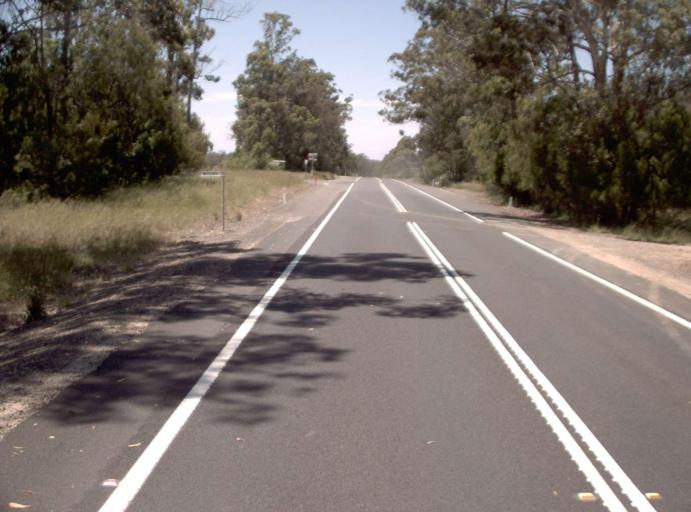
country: AU
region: Victoria
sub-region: East Gippsland
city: Lakes Entrance
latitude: -37.7541
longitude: 148.3216
